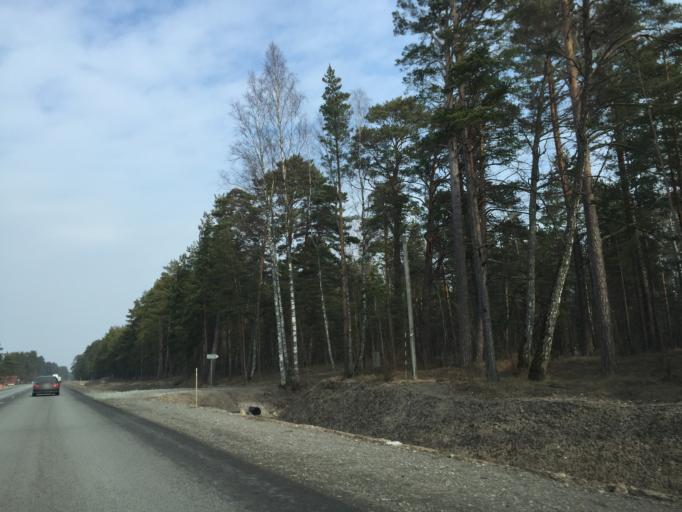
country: LV
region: Salacgrivas
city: Salacgriva
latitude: 57.8080
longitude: 24.3483
